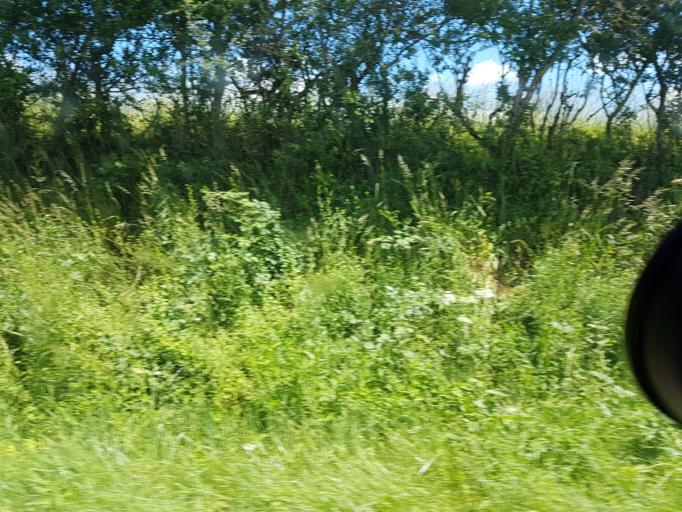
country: FR
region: Bourgogne
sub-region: Departement de Saone-et-Loire
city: Curgy
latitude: 47.0350
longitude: 4.4100
